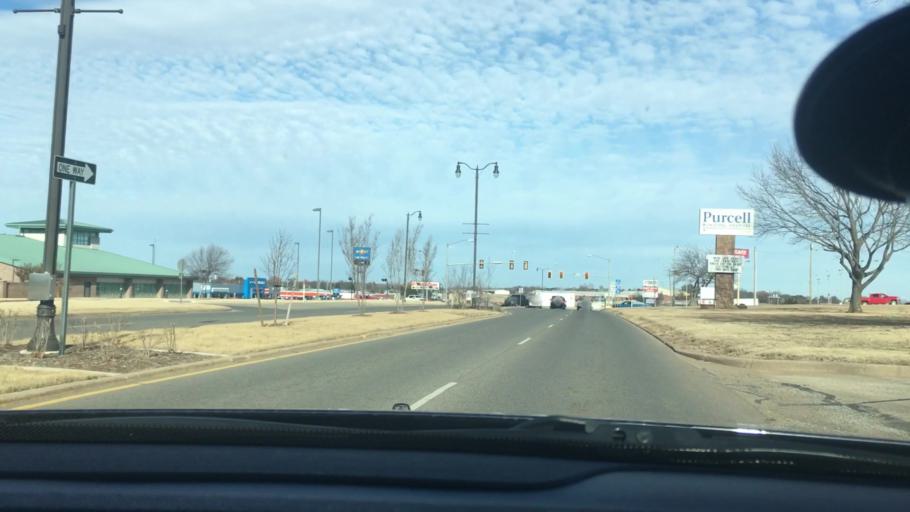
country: US
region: Oklahoma
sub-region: McClain County
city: Purcell
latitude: 35.0283
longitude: -97.3658
